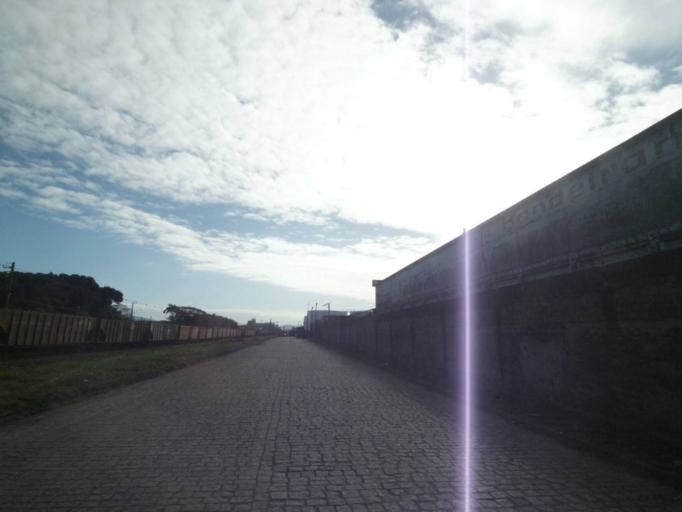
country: BR
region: Parana
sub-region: Paranagua
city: Paranagua
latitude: -25.5205
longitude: -48.5271
